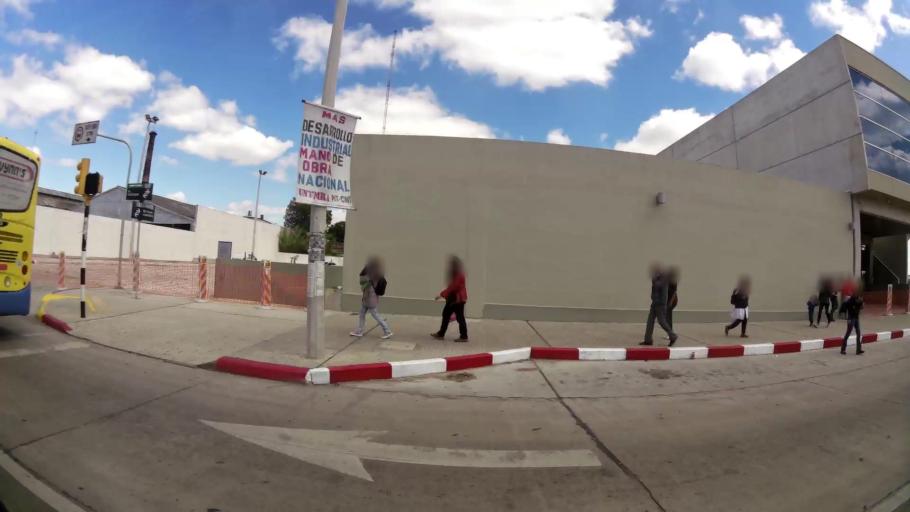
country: UY
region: Montevideo
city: Montevideo
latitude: -34.8561
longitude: -56.1324
